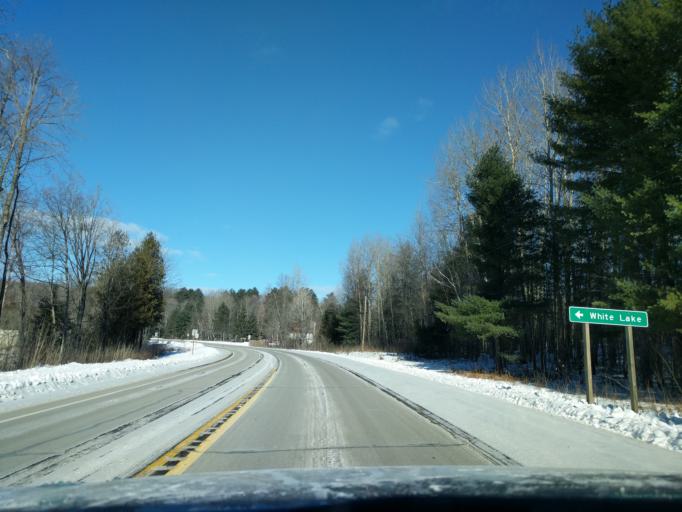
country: US
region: Wisconsin
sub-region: Menominee County
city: Keshena
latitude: 45.1247
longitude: -88.6622
